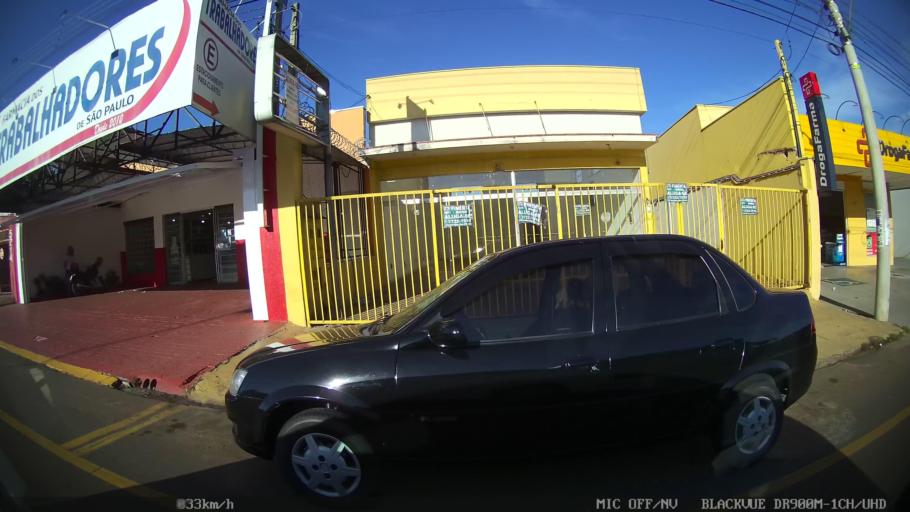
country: BR
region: Sao Paulo
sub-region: Franca
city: Franca
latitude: -20.5086
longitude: -47.3993
